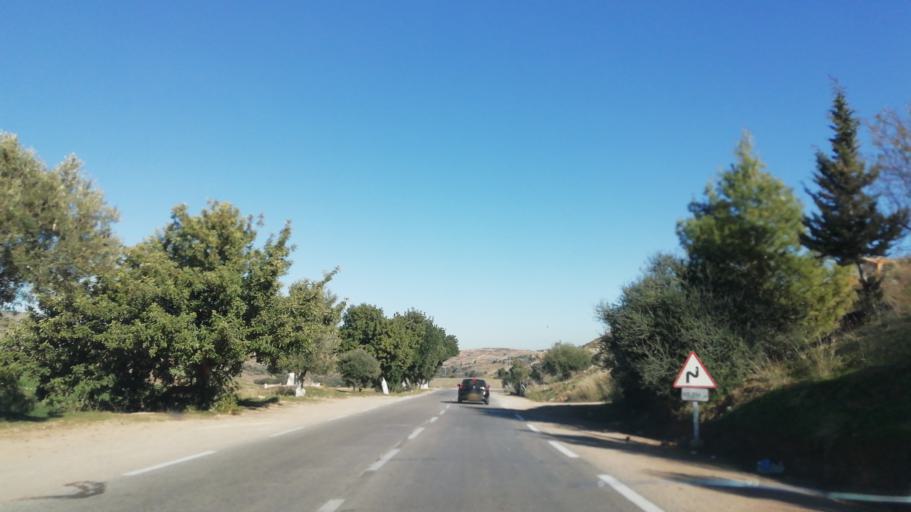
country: DZ
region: Tlemcen
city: Beni Mester
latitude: 34.8350
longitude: -1.4944
